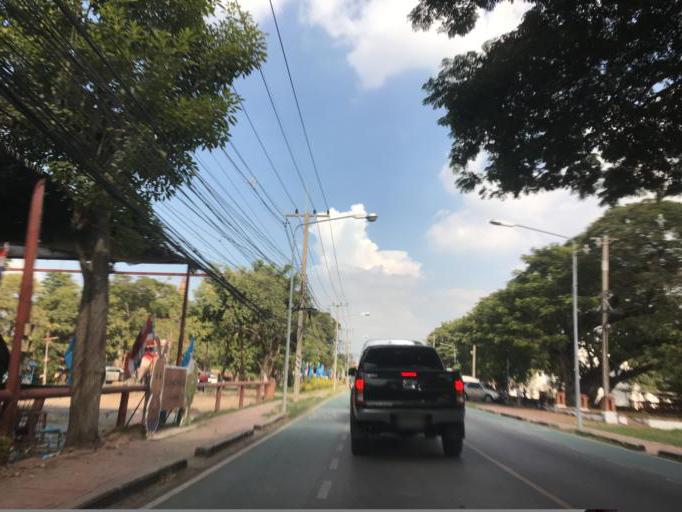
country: TH
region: Phra Nakhon Si Ayutthaya
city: Phra Nakhon Si Ayutthaya
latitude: 14.3521
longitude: 100.5587
